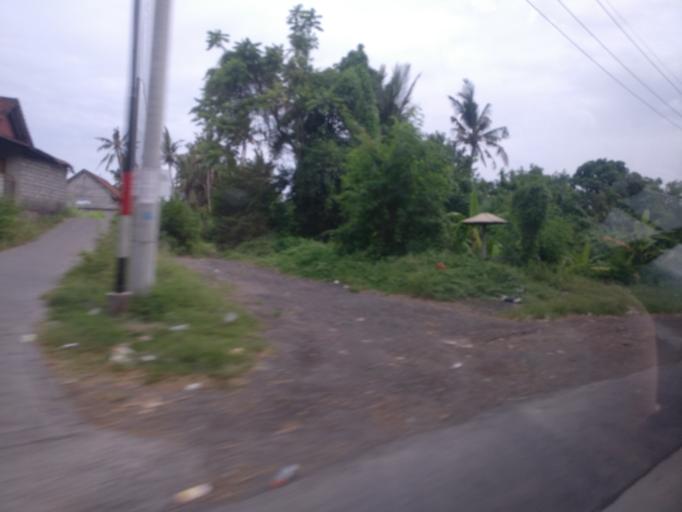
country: ID
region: Bali
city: Banjar Pasekan
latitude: -8.5924
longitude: 115.3406
